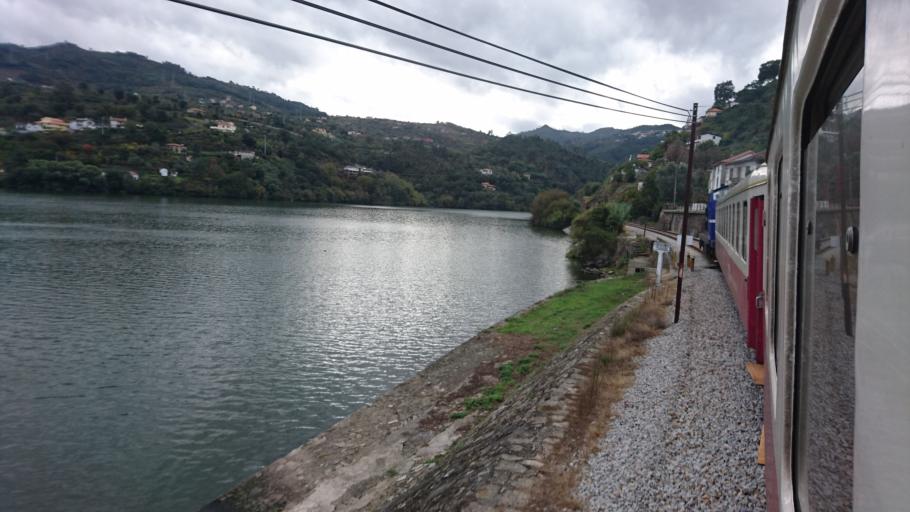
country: PT
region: Viseu
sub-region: Resende
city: Resende
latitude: 41.1058
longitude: -8.0178
